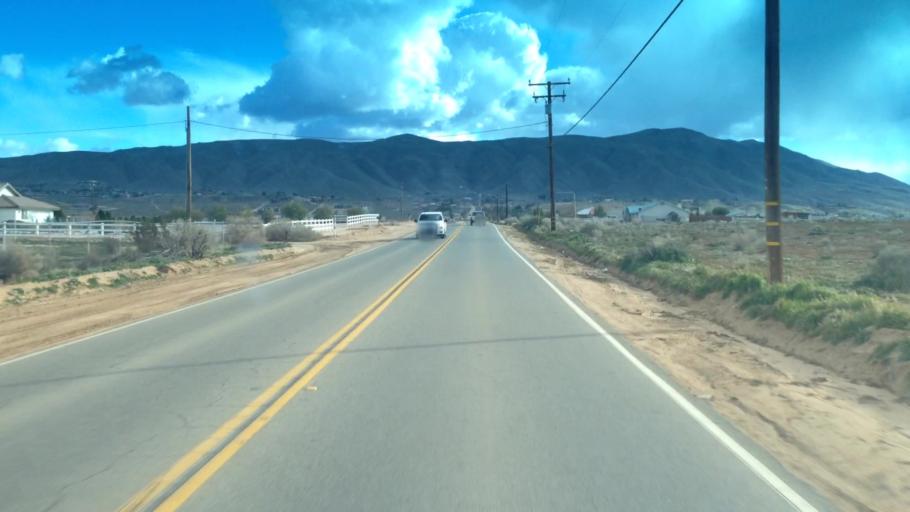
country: US
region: California
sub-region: San Bernardino County
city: Apple Valley
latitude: 34.4487
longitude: -117.1727
